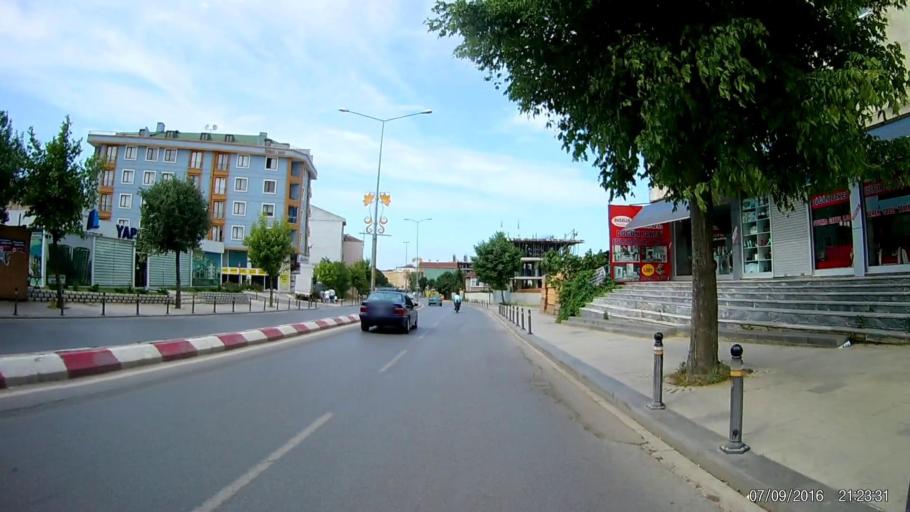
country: TR
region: Istanbul
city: Sultanbeyli
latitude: 40.9736
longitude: 29.2638
